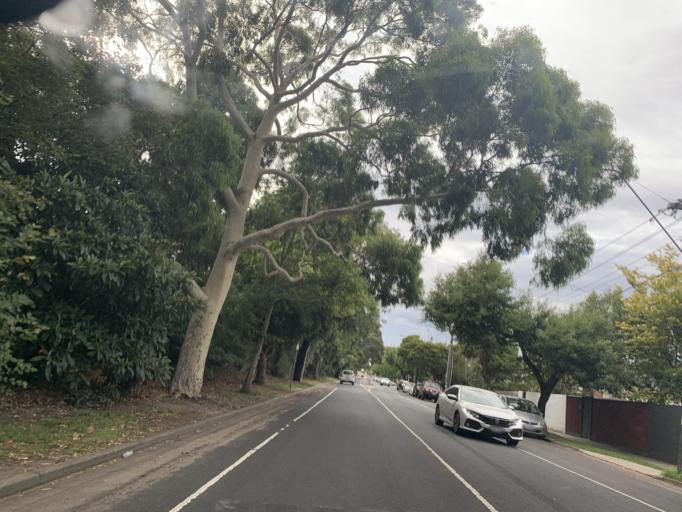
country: AU
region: Victoria
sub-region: Stonnington
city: Malvern East
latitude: -37.8719
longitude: 145.0354
